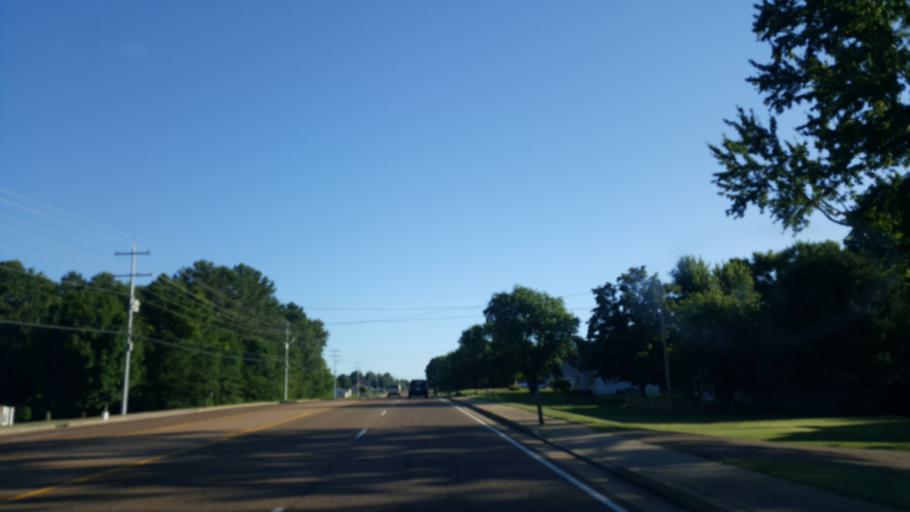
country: US
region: Tennessee
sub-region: Henderson County
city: Lexington
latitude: 35.6743
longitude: -88.3849
